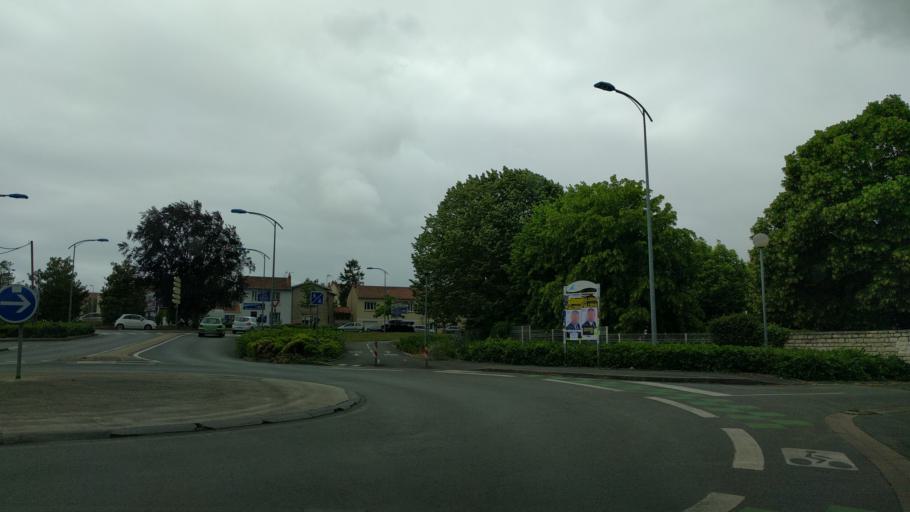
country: FR
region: Poitou-Charentes
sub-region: Departement de la Charente-Maritime
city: La Rochelle
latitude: 46.1700
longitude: -1.1466
